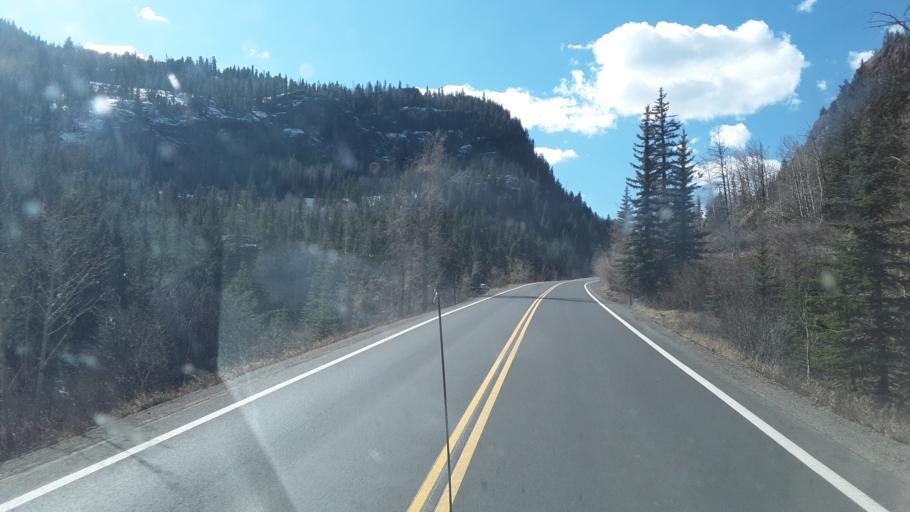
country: US
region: Colorado
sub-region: Mineral County
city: Creede
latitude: 37.5713
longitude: -106.7575
